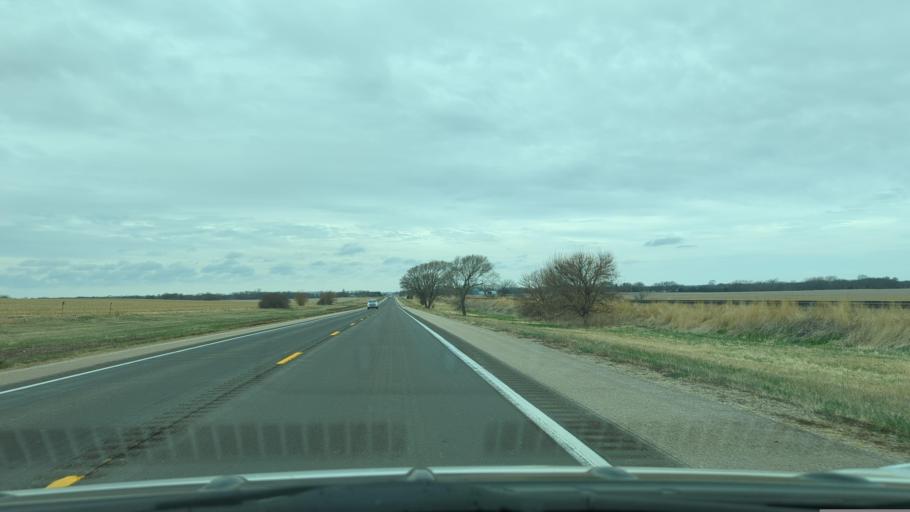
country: US
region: Nebraska
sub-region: Lancaster County
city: Waverly
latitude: 40.9447
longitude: -96.4685
